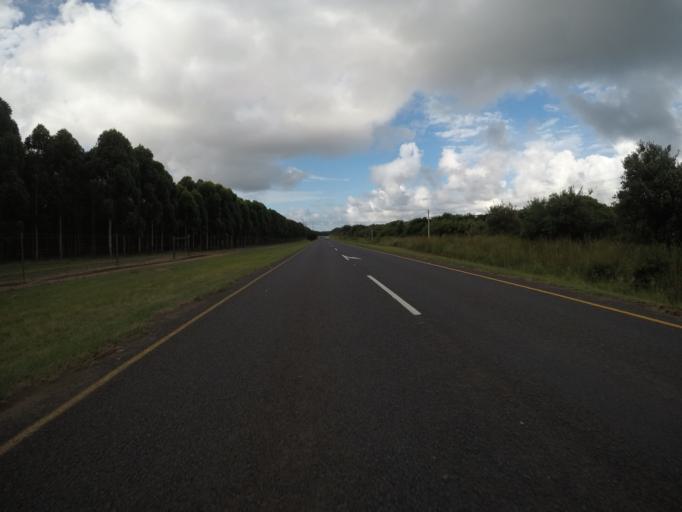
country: ZA
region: KwaZulu-Natal
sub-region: uMkhanyakude District Municipality
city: Mtubatuba
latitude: -28.3763
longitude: 32.2511
